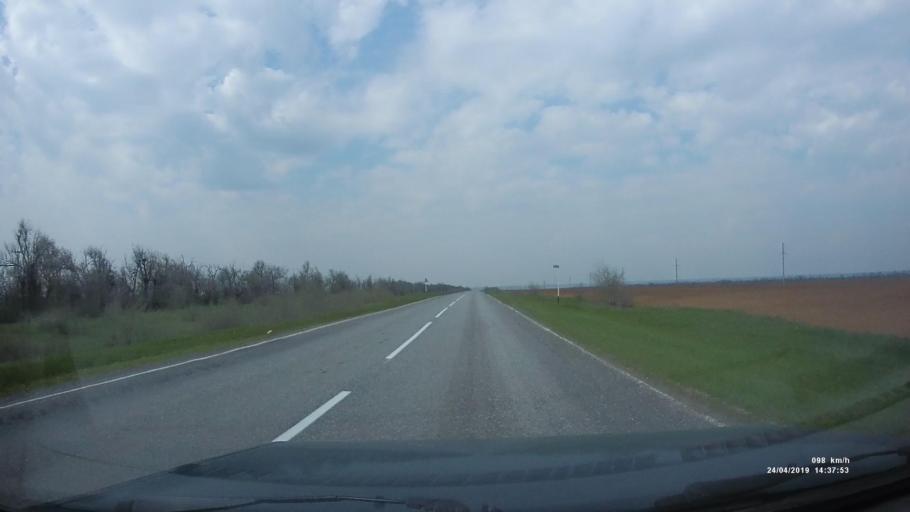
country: RU
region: Rostov
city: Remontnoye
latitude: 46.3930
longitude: 43.8862
